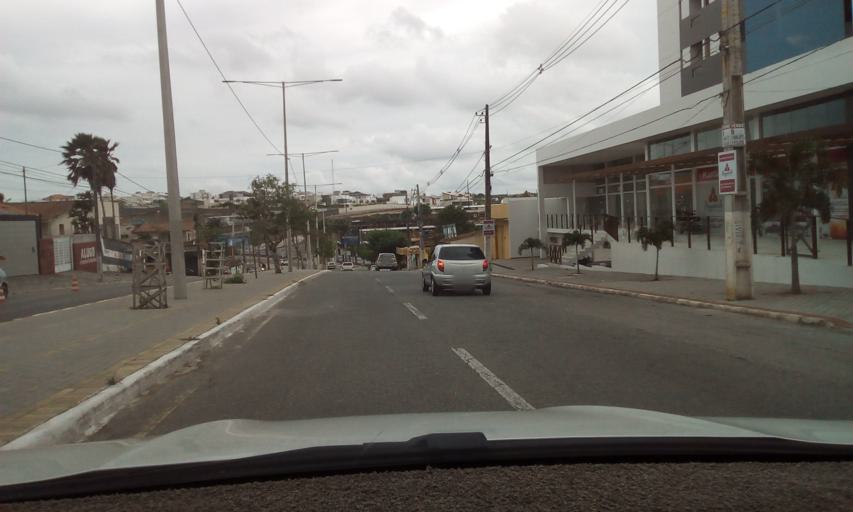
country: BR
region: Paraiba
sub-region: Campina Grande
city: Campina Grande
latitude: -7.2059
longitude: -35.8750
